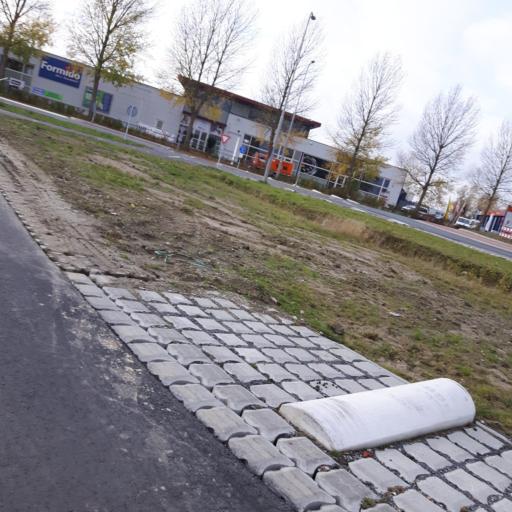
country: NL
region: Zeeland
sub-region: Gemeente Goes
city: Goes
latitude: 51.4822
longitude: 3.8198
